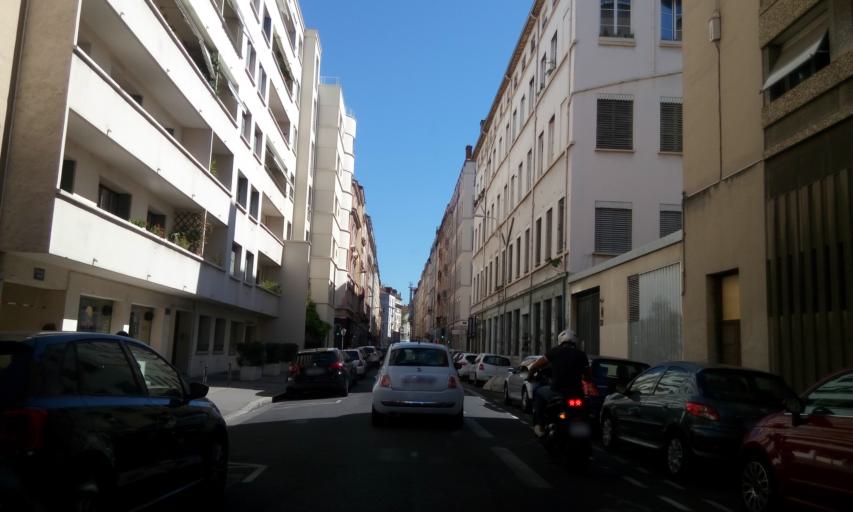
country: FR
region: Rhone-Alpes
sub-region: Departement du Rhone
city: Lyon
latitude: 45.7689
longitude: 4.8532
